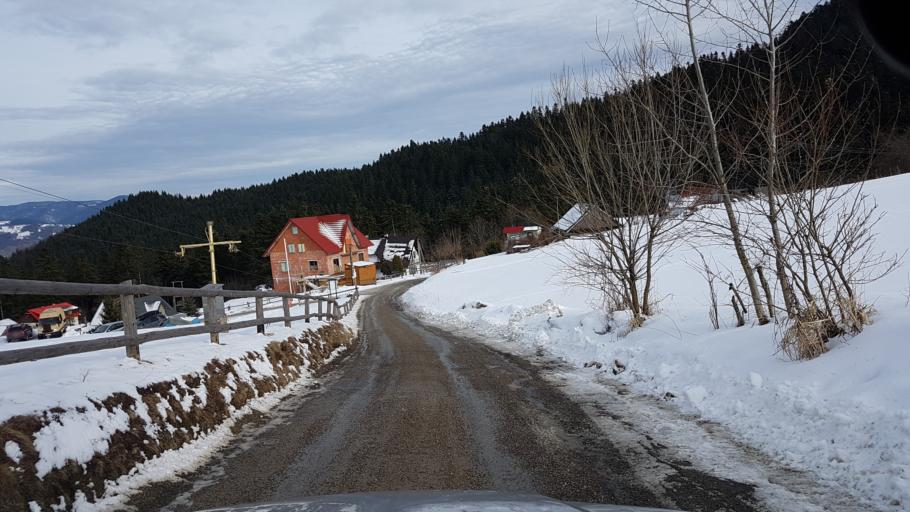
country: PL
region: Lesser Poland Voivodeship
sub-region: Powiat nowosadecki
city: Rytro
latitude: 49.4169
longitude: 20.6398
